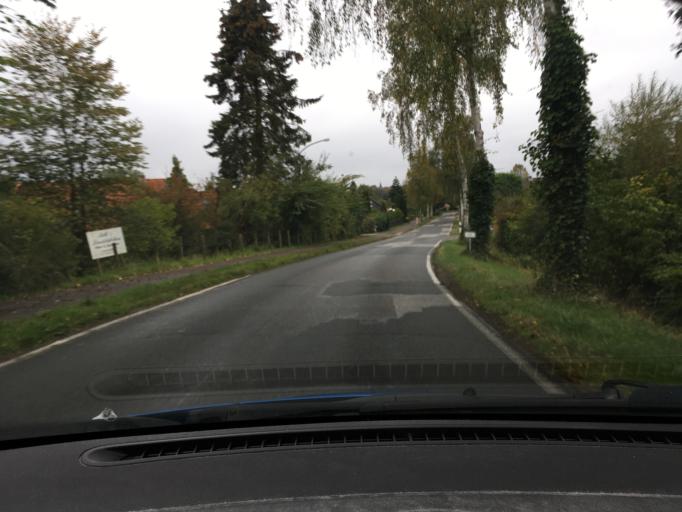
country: DE
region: Schleswig-Holstein
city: Bosau
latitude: 54.1025
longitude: 10.4328
